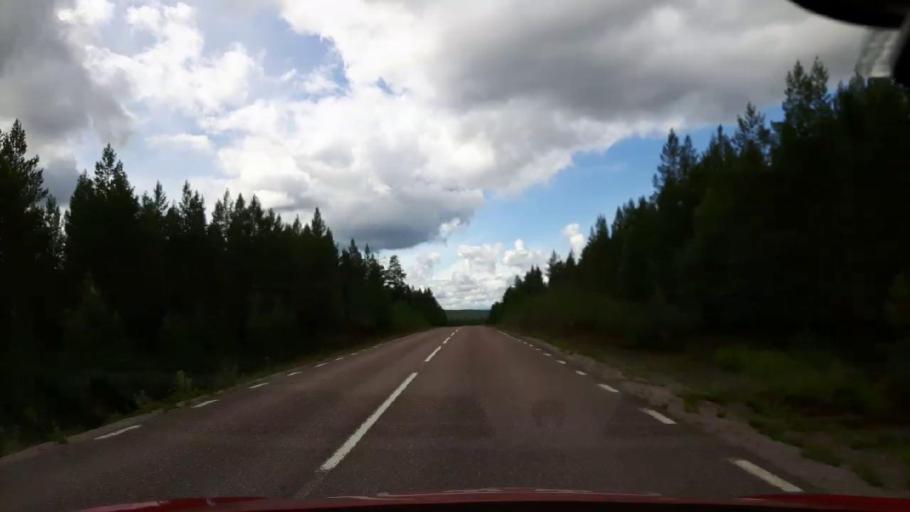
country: SE
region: Jaemtland
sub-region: Harjedalens Kommun
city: Sveg
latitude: 61.8272
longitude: 13.8730
